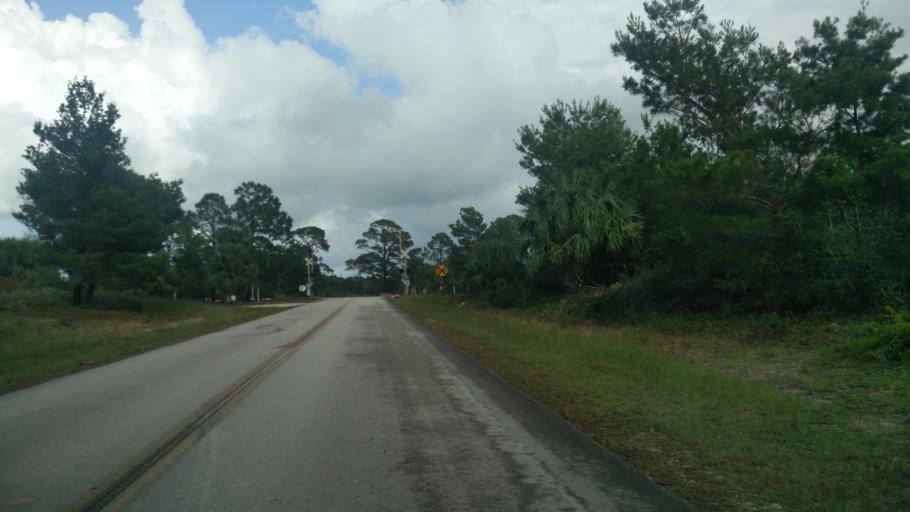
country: US
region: Florida
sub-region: Palm Beach County
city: Tequesta
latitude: 27.0113
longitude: -80.1142
